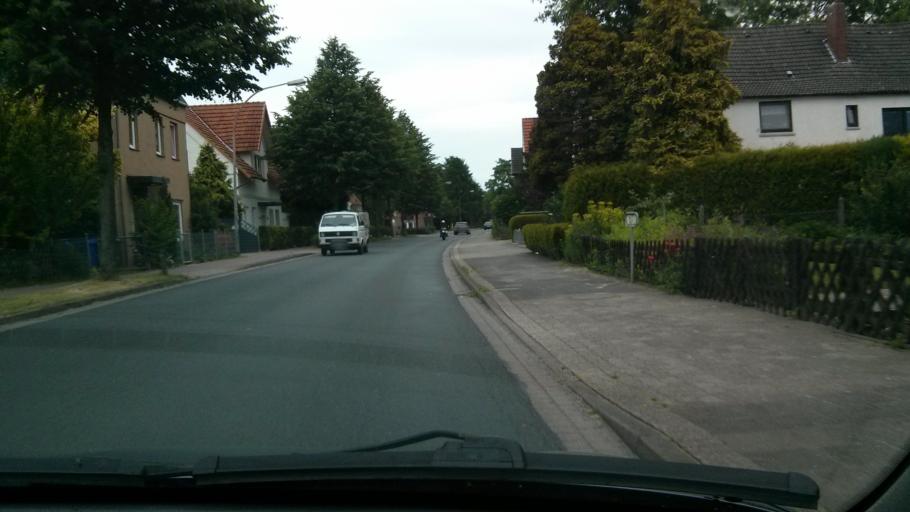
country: DE
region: Lower Saxony
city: Loxstedt
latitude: 53.4671
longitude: 8.6426
